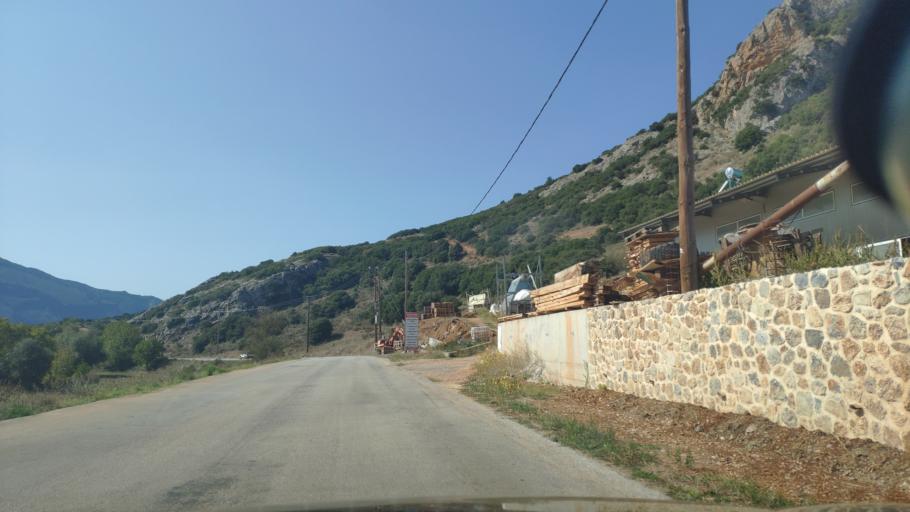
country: GR
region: Peloponnese
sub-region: Nomos Korinthias
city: Nemea
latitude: 37.9003
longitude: 22.5194
